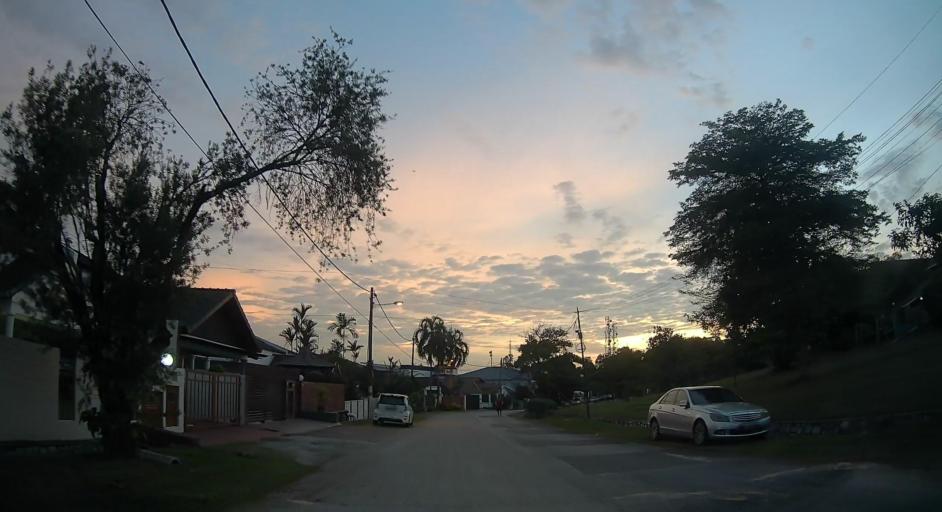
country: MY
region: Selangor
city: Subang Jaya
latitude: 3.0700
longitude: 101.5749
